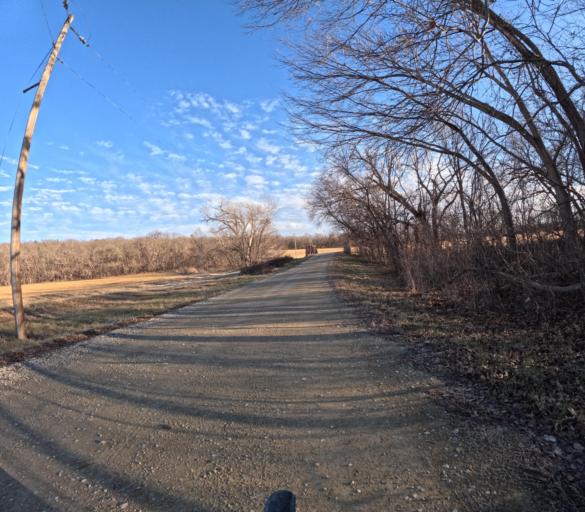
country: US
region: Kansas
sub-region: Riley County
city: Ogden
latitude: 39.2129
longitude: -96.6773
